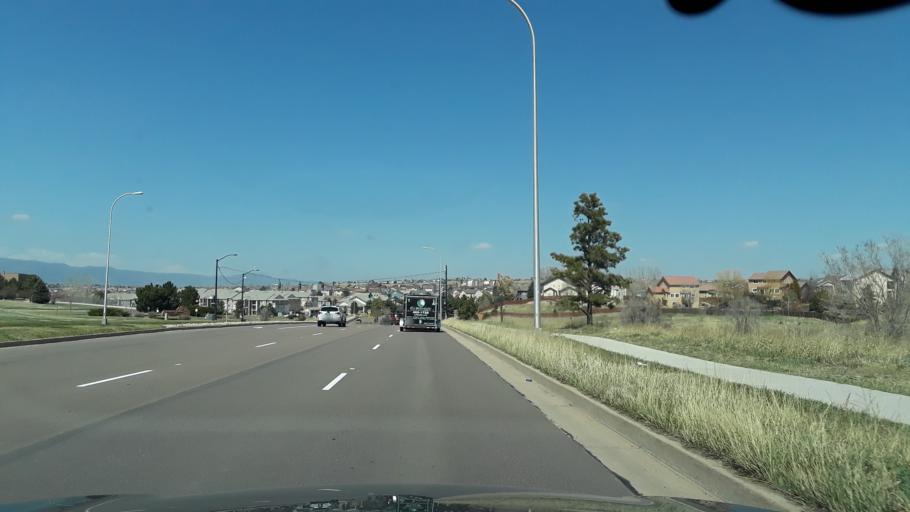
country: US
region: Colorado
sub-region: El Paso County
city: Cimarron Hills
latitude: 38.9273
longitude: -104.7393
